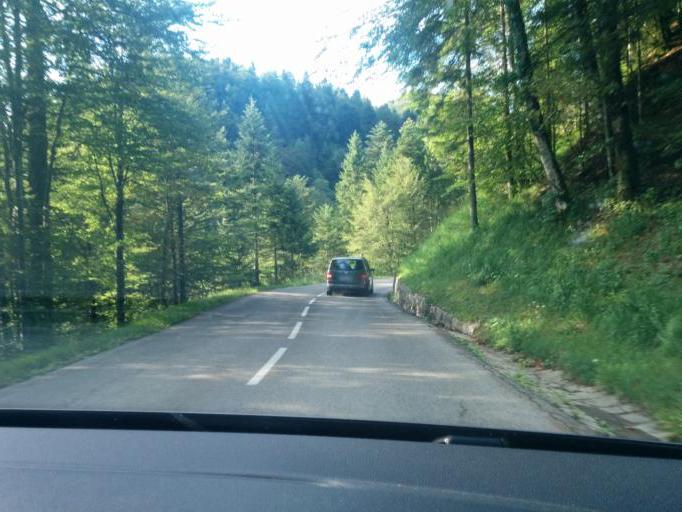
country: FR
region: Franche-Comte
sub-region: Departement du Jura
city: Saint-Lupicin
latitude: 46.4472
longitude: 5.8060
